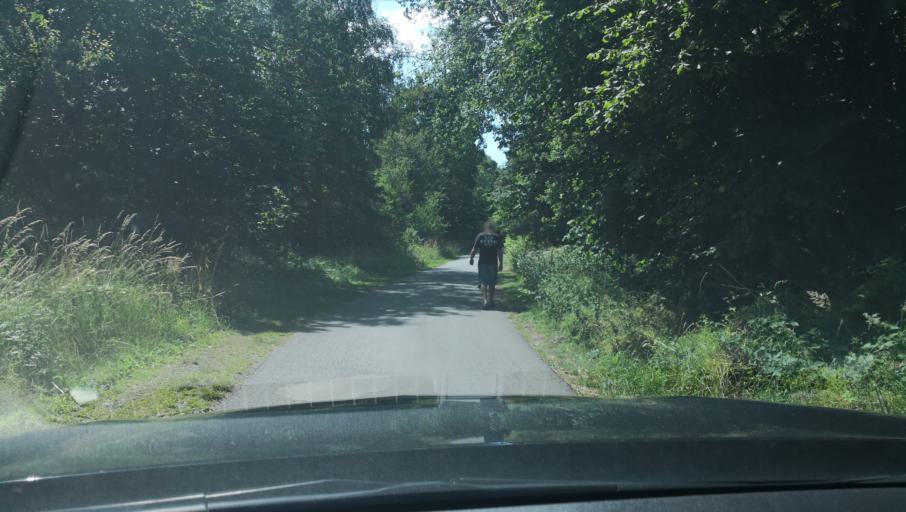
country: SE
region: Skane
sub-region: Ystads Kommun
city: Kopingebro
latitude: 55.3832
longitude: 14.1455
